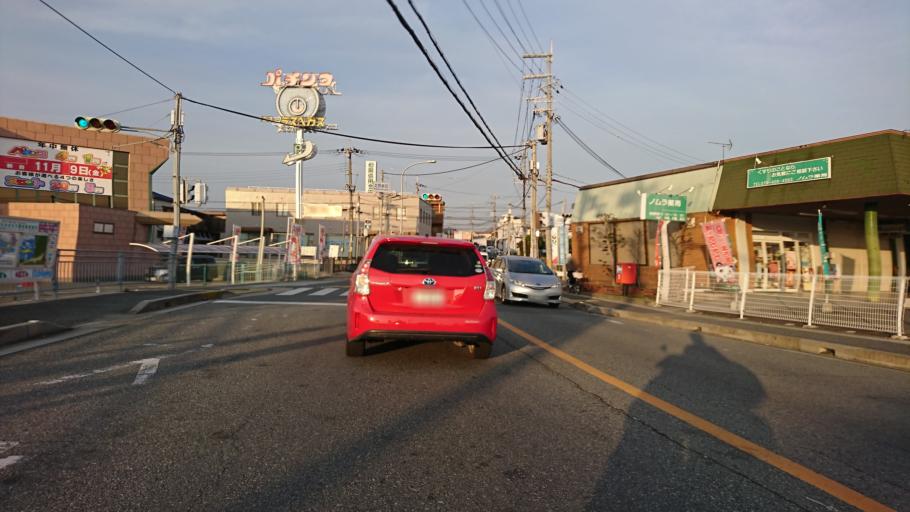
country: JP
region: Hyogo
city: Kakogawacho-honmachi
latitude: 34.7580
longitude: 134.8739
